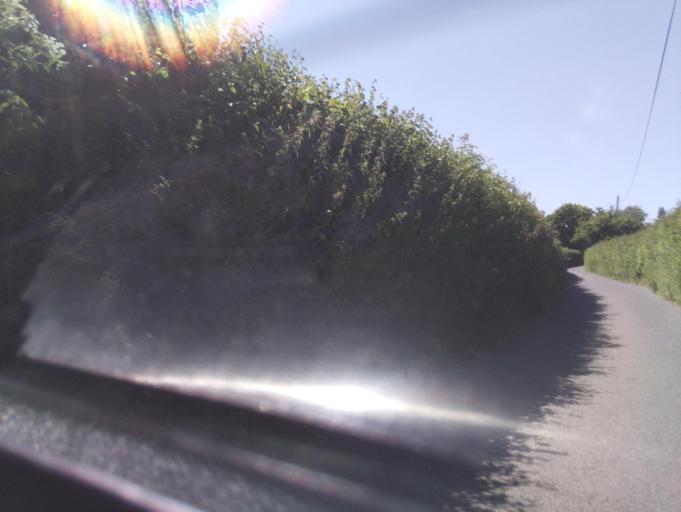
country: GB
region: England
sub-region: Devon
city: Marldon
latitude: 50.4806
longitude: -3.6058
